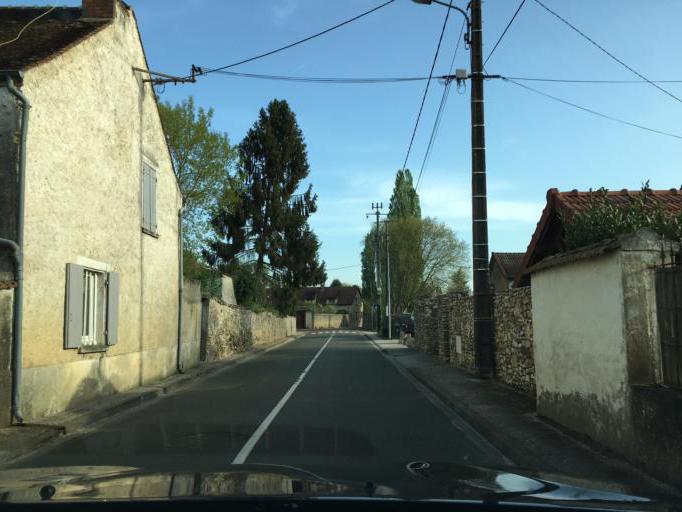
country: FR
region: Centre
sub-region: Departement d'Eure-et-Loir
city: Epernon
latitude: 48.6358
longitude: 1.6807
